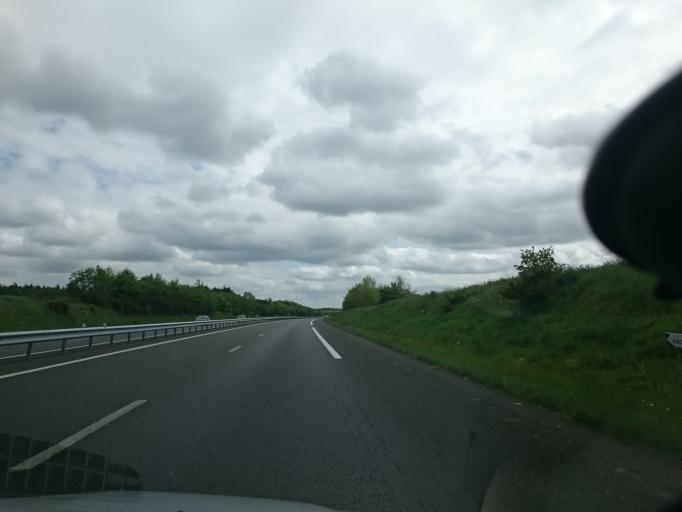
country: FR
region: Brittany
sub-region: Departement d'Ille-et-Vilaine
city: Saint-Sauveur-des-Landes
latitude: 48.3487
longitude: -1.2985
